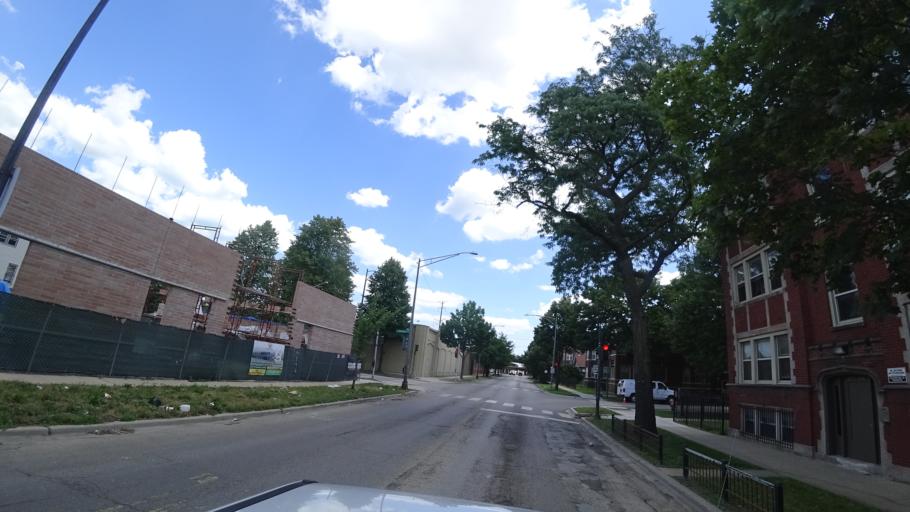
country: US
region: Illinois
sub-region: Cook County
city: Chicago
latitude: 41.7729
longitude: -87.6207
